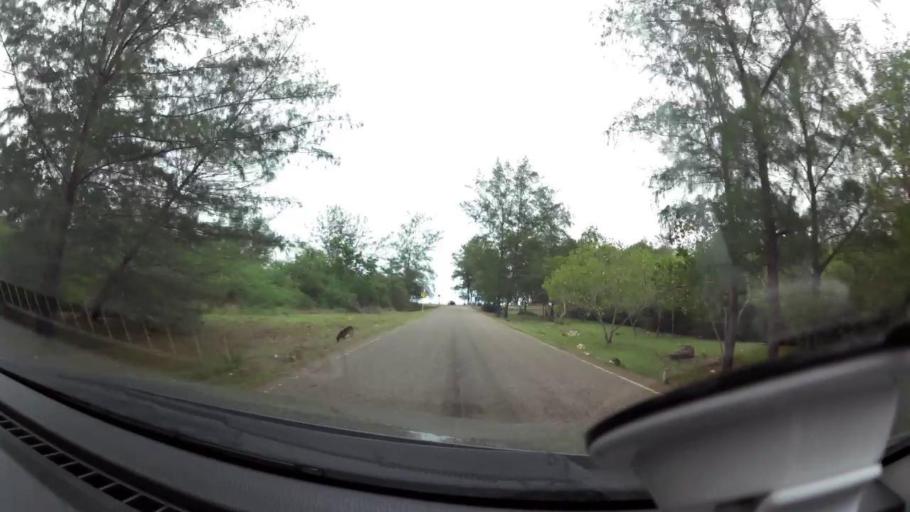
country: TH
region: Prachuap Khiri Khan
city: Pran Buri
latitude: 12.4189
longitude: 99.9829
